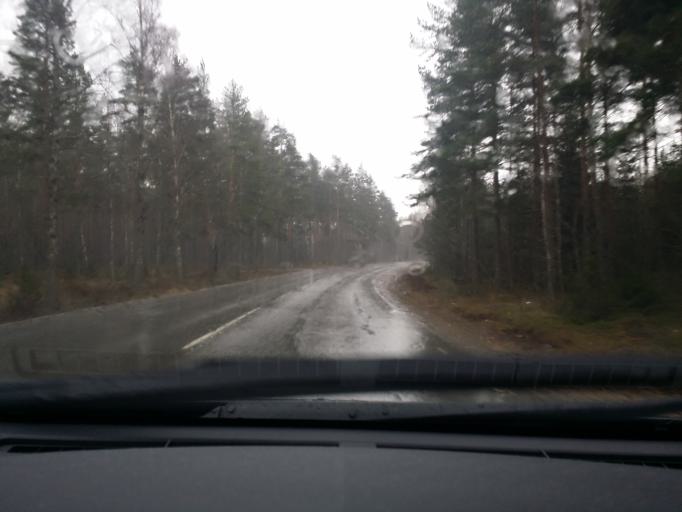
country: SE
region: Soedermanland
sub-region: Eskilstuna Kommun
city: Arla
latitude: 59.3543
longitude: 16.6888
